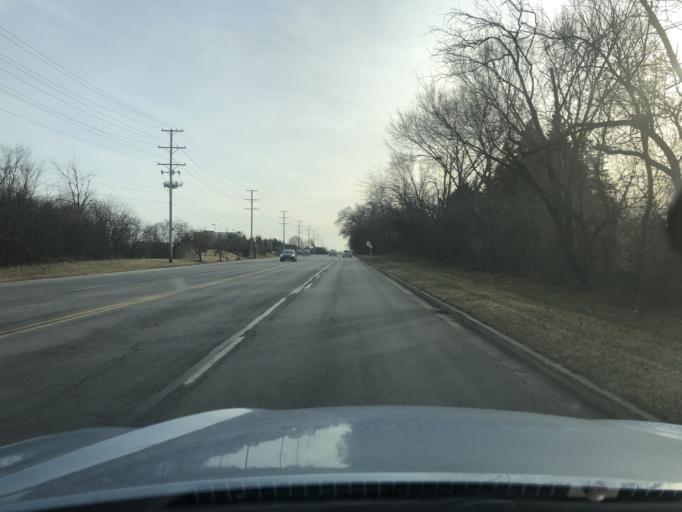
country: US
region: Illinois
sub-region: DuPage County
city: Itasca
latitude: 41.9776
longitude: -87.9982
